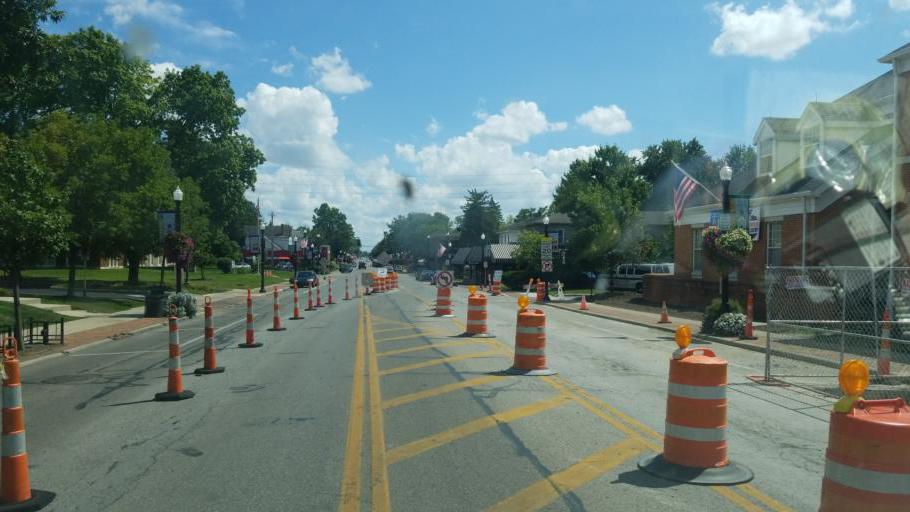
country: US
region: Ohio
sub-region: Franklin County
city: Westerville
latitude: 40.1251
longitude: -82.9313
